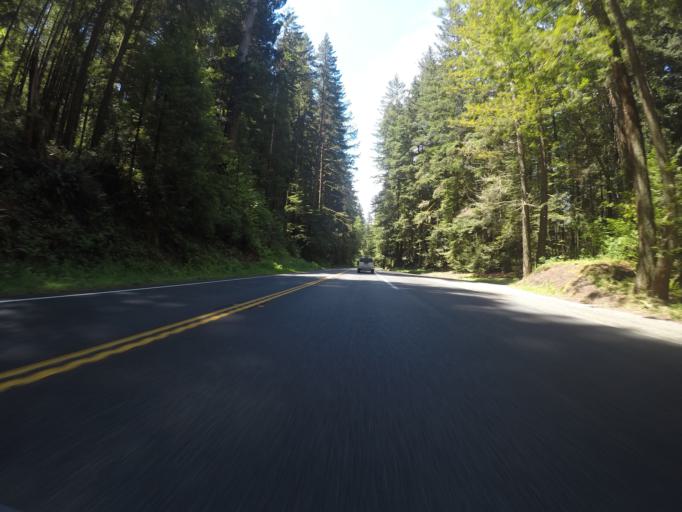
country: US
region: California
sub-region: Del Norte County
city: Bertsch-Oceanview
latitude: 41.8078
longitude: -124.1324
